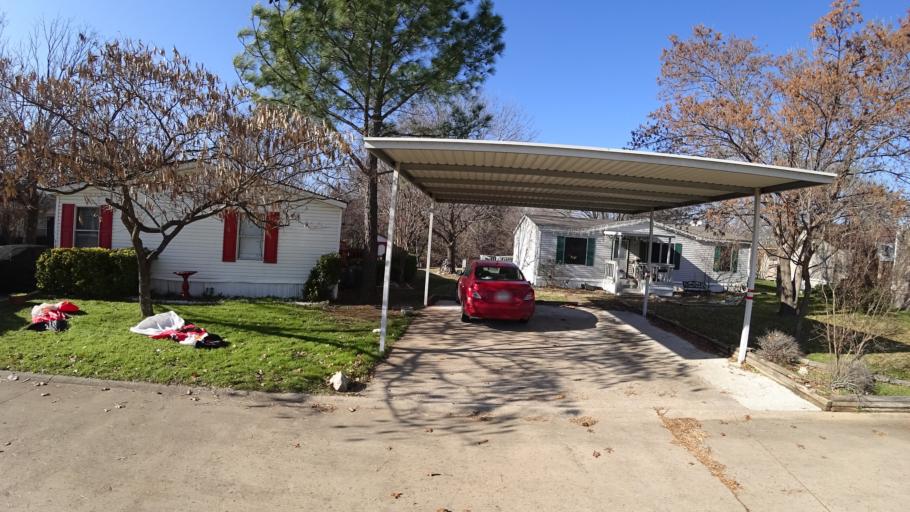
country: US
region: Texas
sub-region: Dallas County
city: Coppell
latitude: 32.9902
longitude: -97.0200
